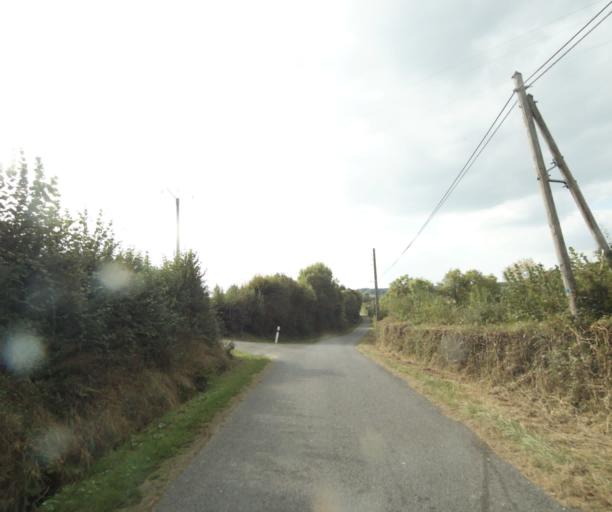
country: FR
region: Bourgogne
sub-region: Departement de Saone-et-Loire
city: Palinges
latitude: 46.5279
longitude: 4.2799
